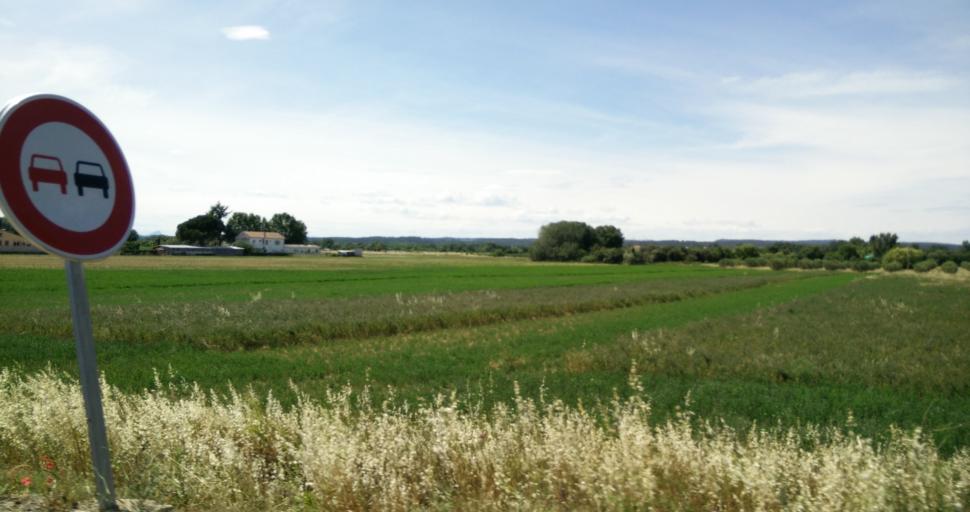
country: FR
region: Languedoc-Roussillon
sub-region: Departement du Gard
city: Aubord
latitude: 43.7426
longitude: 4.2955
